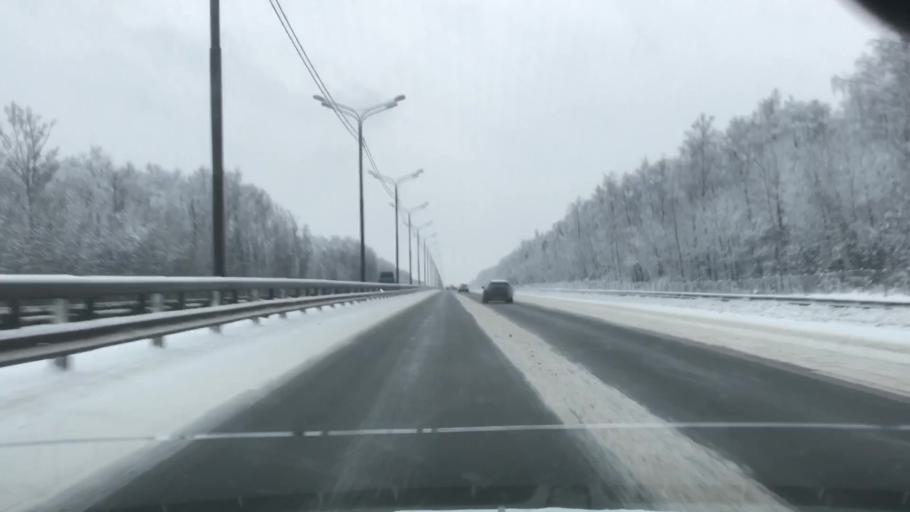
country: RU
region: Moskovskaya
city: Belyye Stolby
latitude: 55.3032
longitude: 37.8333
